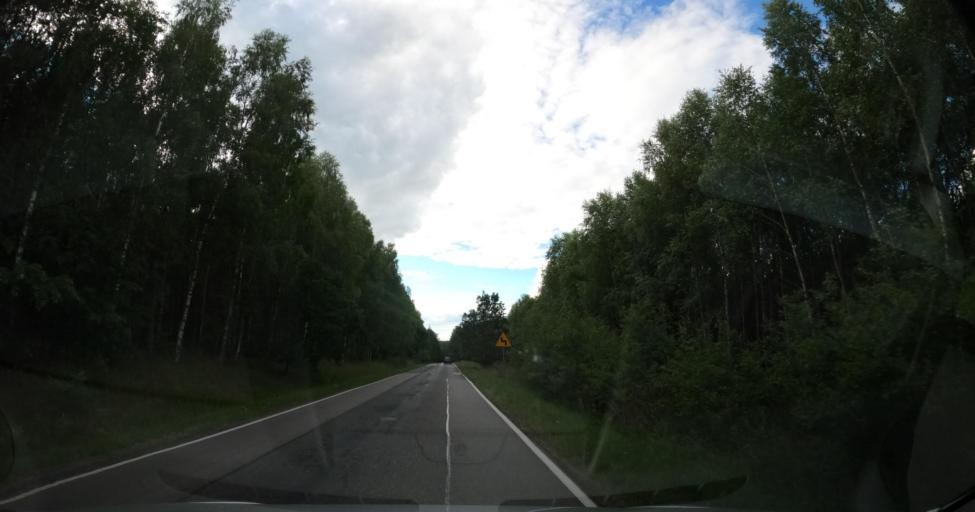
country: PL
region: Pomeranian Voivodeship
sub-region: Powiat bytowski
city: Czarna Dabrowka
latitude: 54.3716
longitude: 17.5012
